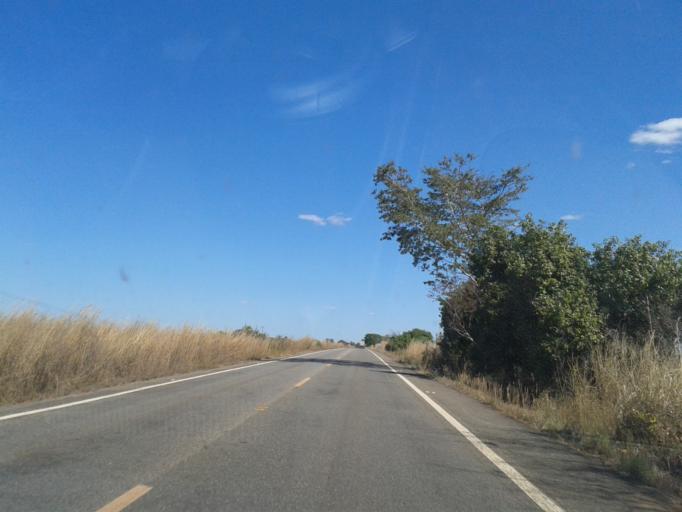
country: BR
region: Goias
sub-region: Sao Miguel Do Araguaia
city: Sao Miguel do Araguaia
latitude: -13.5997
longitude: -50.3192
